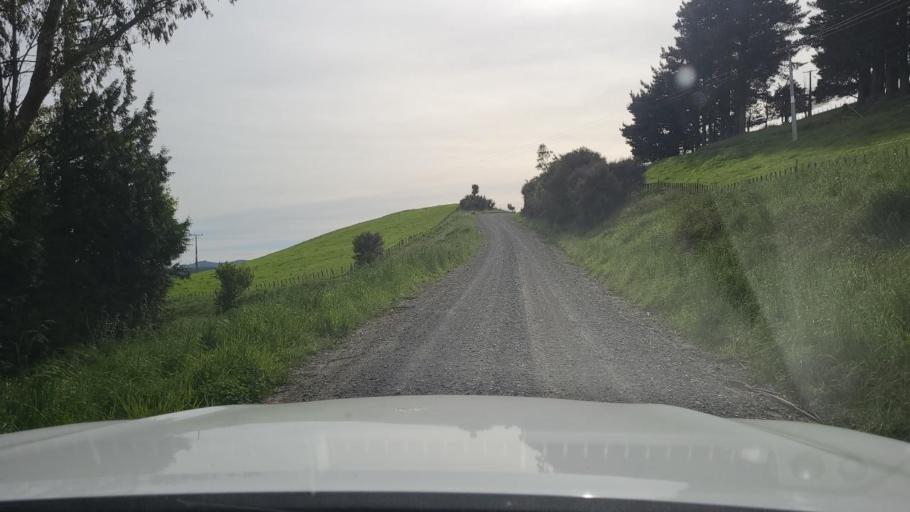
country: NZ
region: Hawke's Bay
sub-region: Napier City
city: Taradale
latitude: -39.3009
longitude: 176.6389
